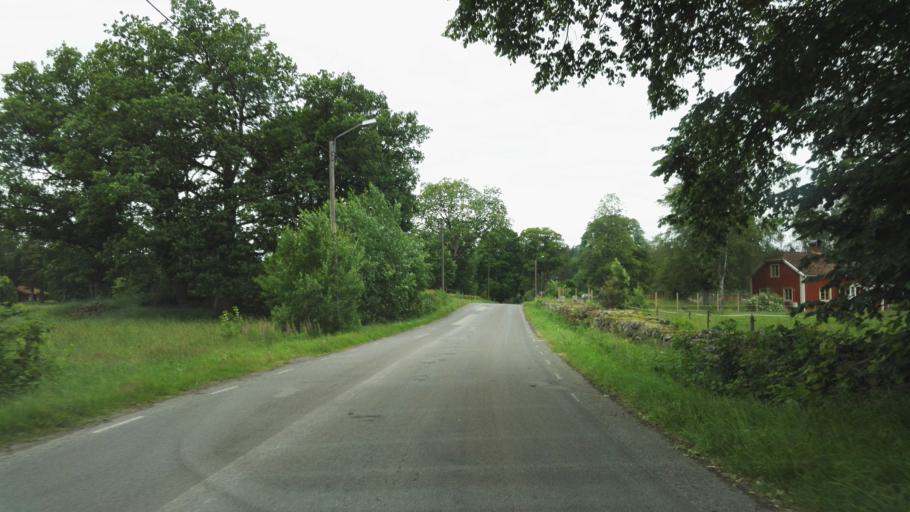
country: SE
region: Kronoberg
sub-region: Vaxjo Kommun
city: Rottne
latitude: 57.0920
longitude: 14.7983
